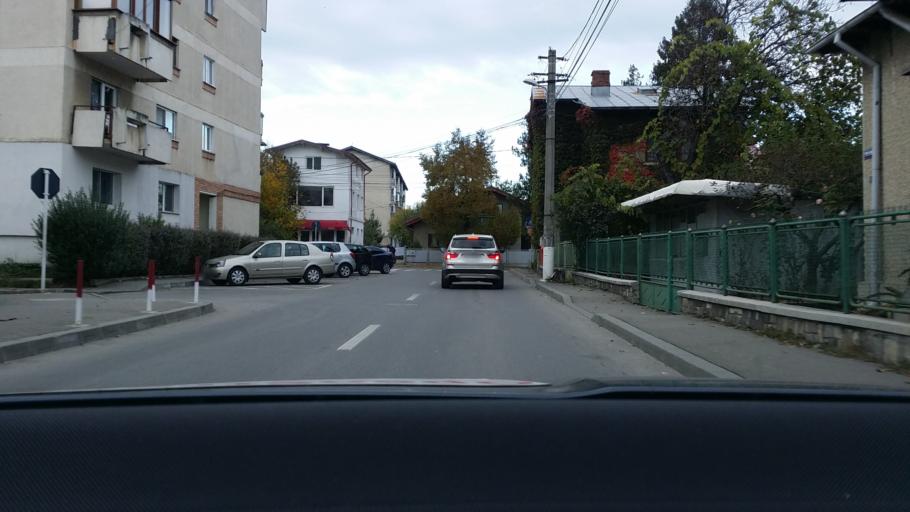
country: RO
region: Prahova
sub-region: Municipiul Campina
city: Campina
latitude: 45.1237
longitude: 25.7392
